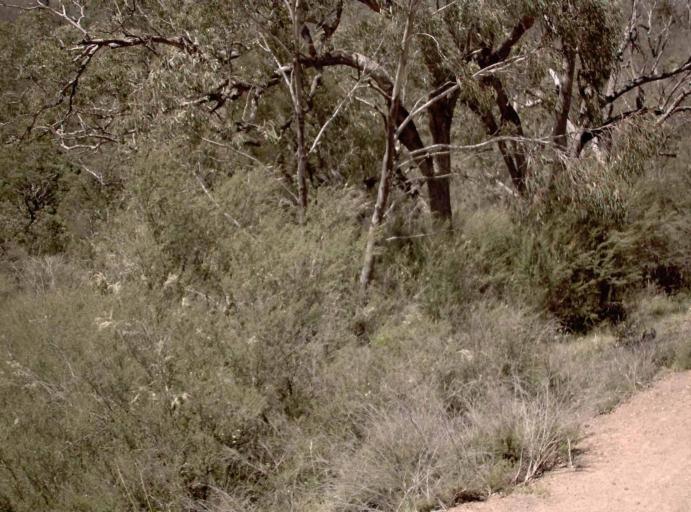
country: AU
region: New South Wales
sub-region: Snowy River
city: Jindabyne
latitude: -37.0366
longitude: 148.5518
